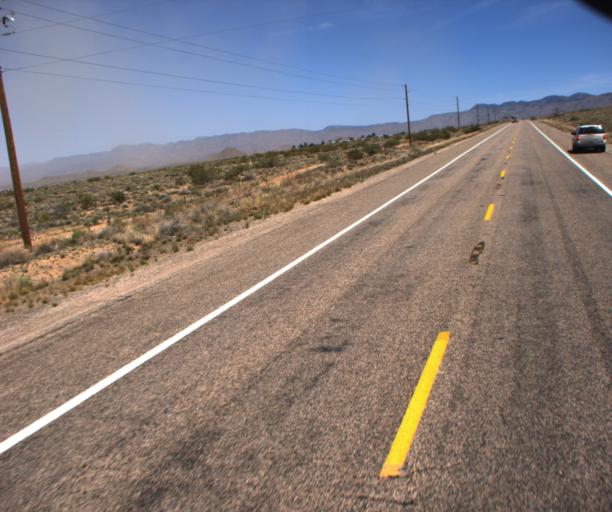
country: US
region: Arizona
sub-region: Mohave County
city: New Kingman-Butler
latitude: 35.3853
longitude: -113.8498
